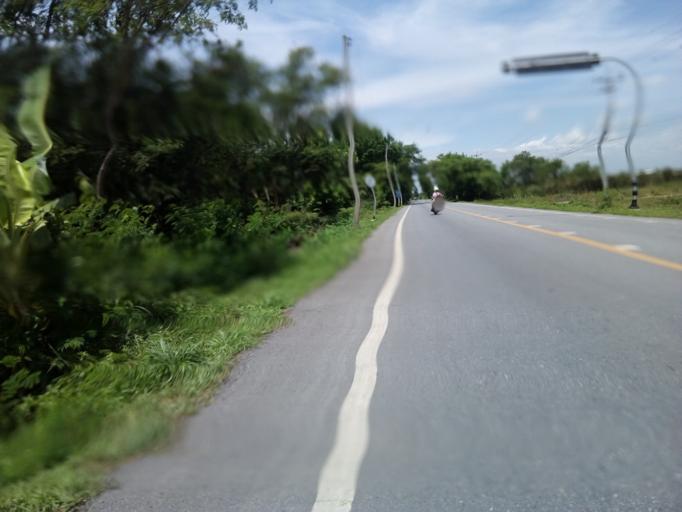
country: TH
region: Pathum Thani
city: Ban Lam Luk Ka
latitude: 14.0158
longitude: 100.8431
